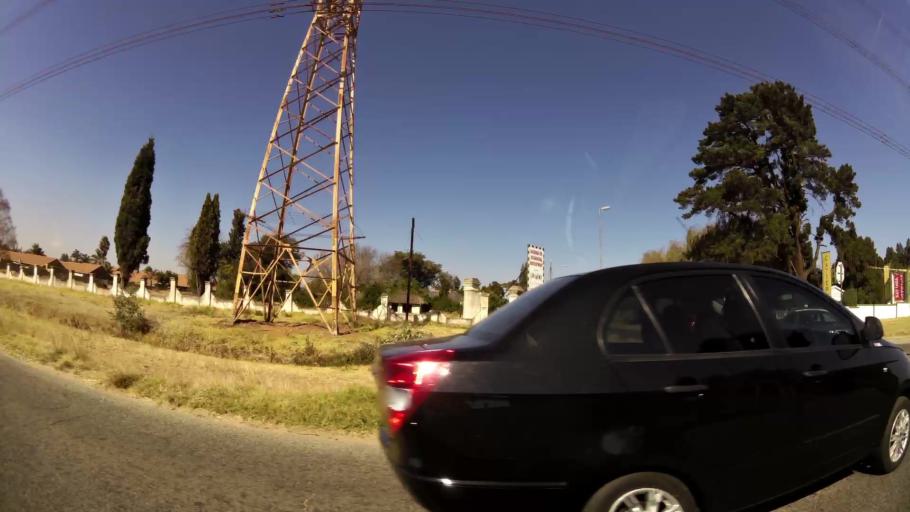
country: ZA
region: Gauteng
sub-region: City of Johannesburg Metropolitan Municipality
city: Modderfontein
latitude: -26.0758
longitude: 28.1981
